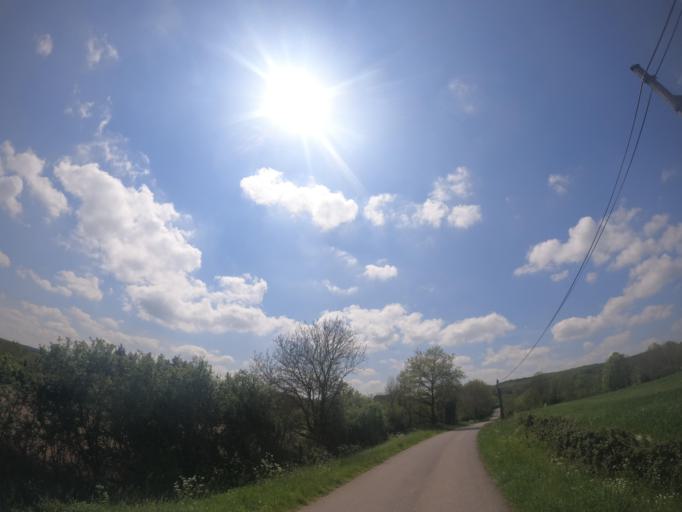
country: FR
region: Poitou-Charentes
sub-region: Departement des Deux-Sevres
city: Saint-Varent
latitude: 46.8563
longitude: -0.2667
